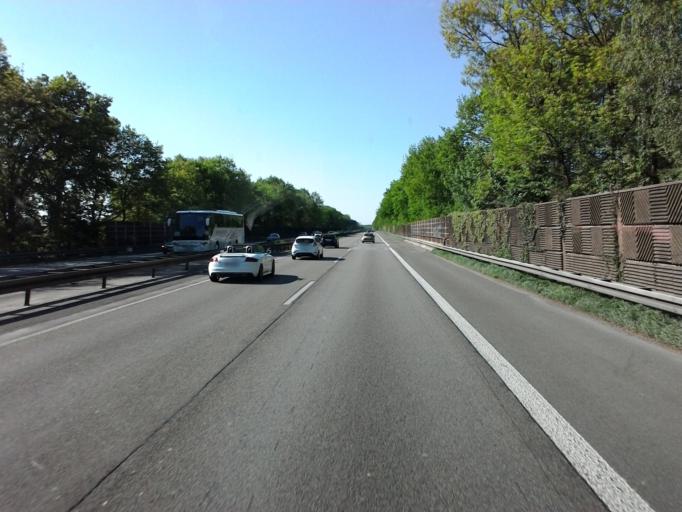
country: DE
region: North Rhine-Westphalia
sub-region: Regierungsbezirk Dusseldorf
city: Dinslaken
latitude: 51.5431
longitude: 6.8259
